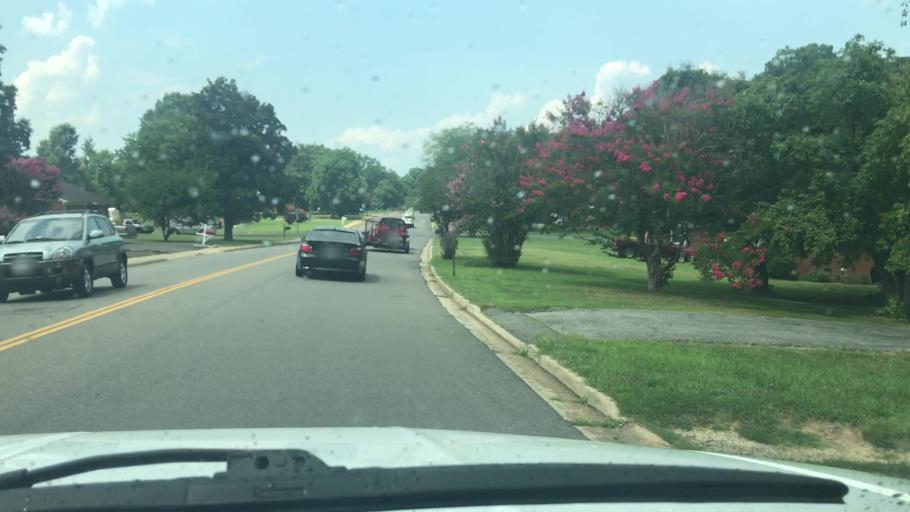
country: US
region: Virginia
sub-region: Henrico County
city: Laurel
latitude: 37.6445
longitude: -77.5423
